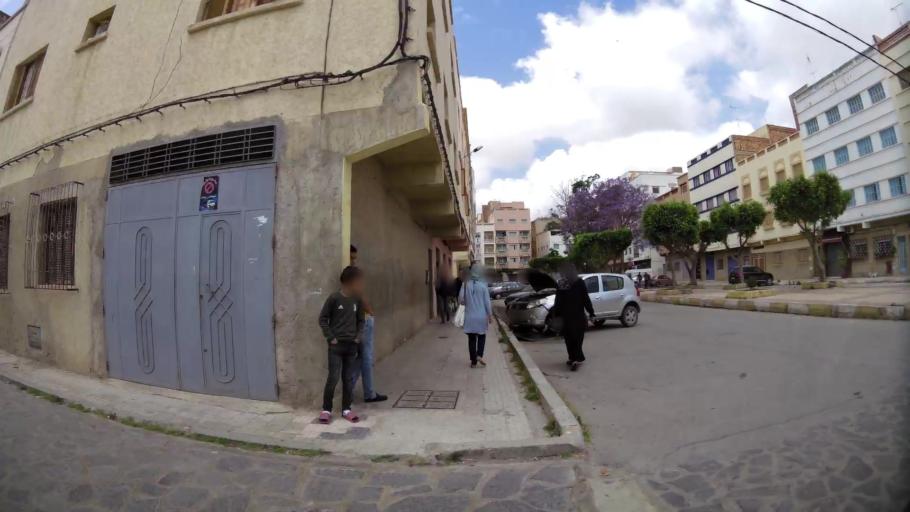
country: MA
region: Oriental
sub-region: Nador
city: Nador
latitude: 35.1695
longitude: -2.9276
